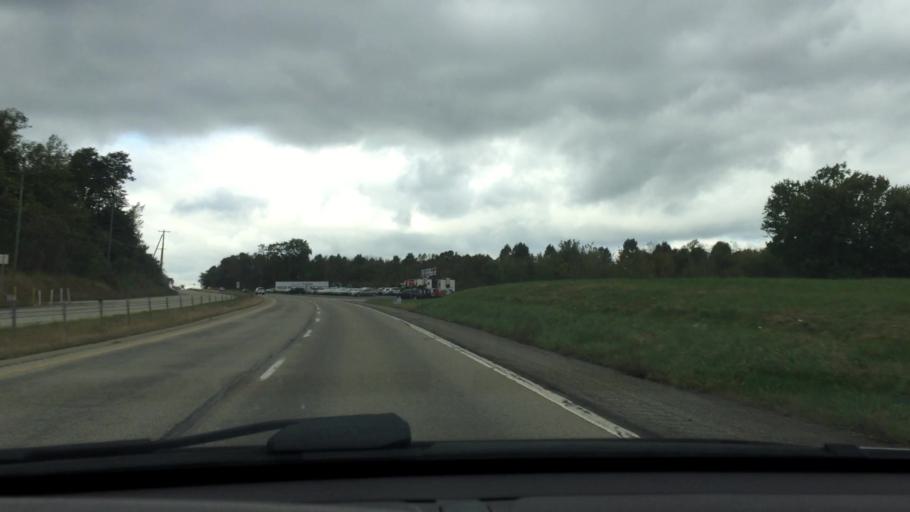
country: US
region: Pennsylvania
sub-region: Westmoreland County
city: Fellsburg
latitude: 40.2175
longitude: -79.8434
